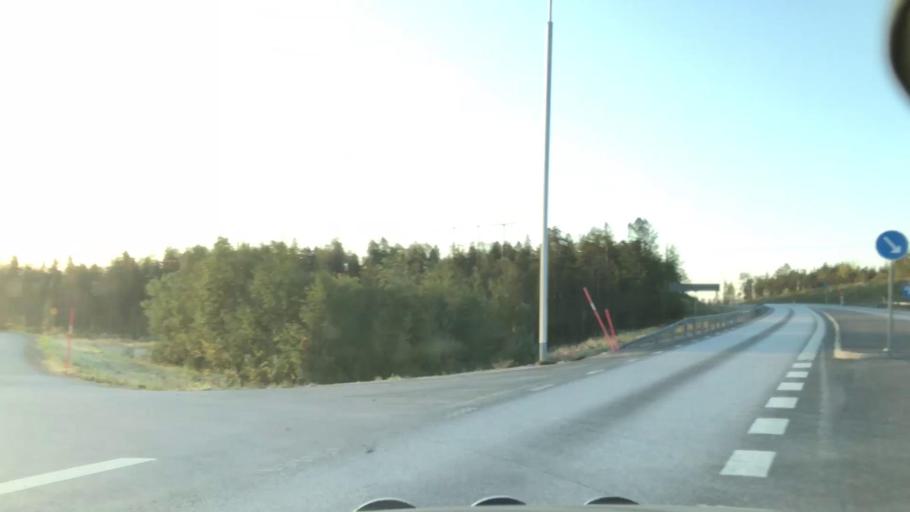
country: SE
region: Norrbotten
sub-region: Gallivare Kommun
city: Malmberget
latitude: 67.6508
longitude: 21.0189
